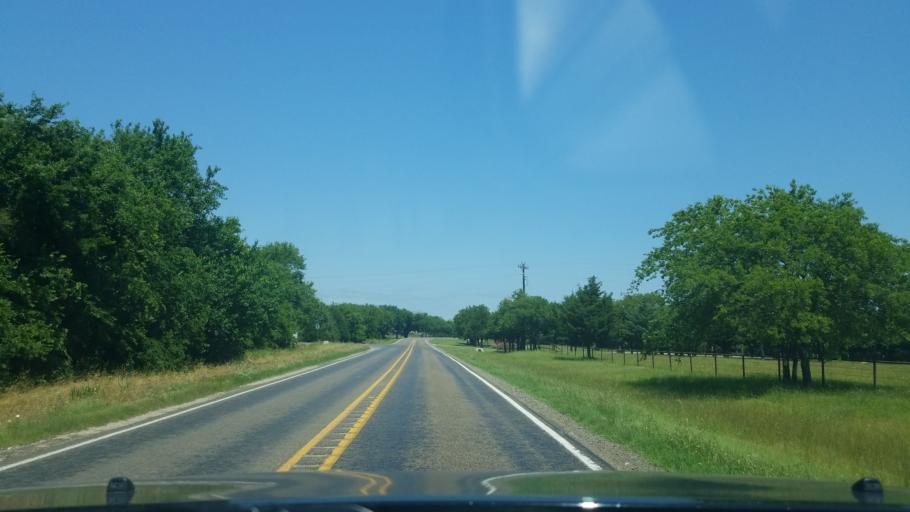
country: US
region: Texas
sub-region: Denton County
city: Krum
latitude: 33.3178
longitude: -97.2377
